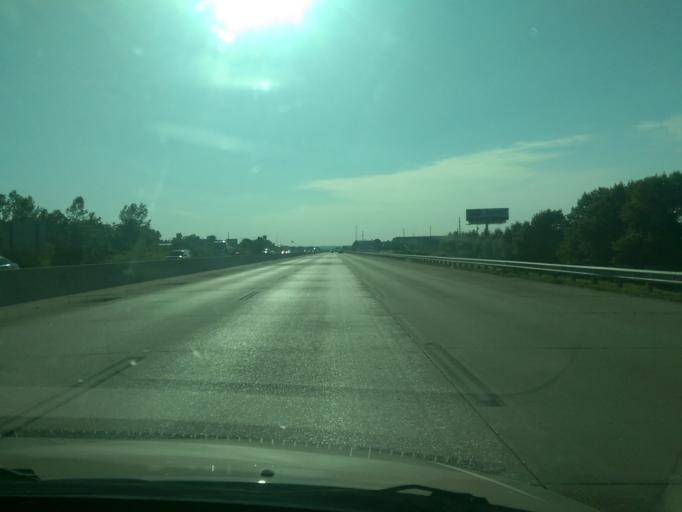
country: US
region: Missouri
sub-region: Jackson County
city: Blue Springs
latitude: 39.0325
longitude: -94.2899
